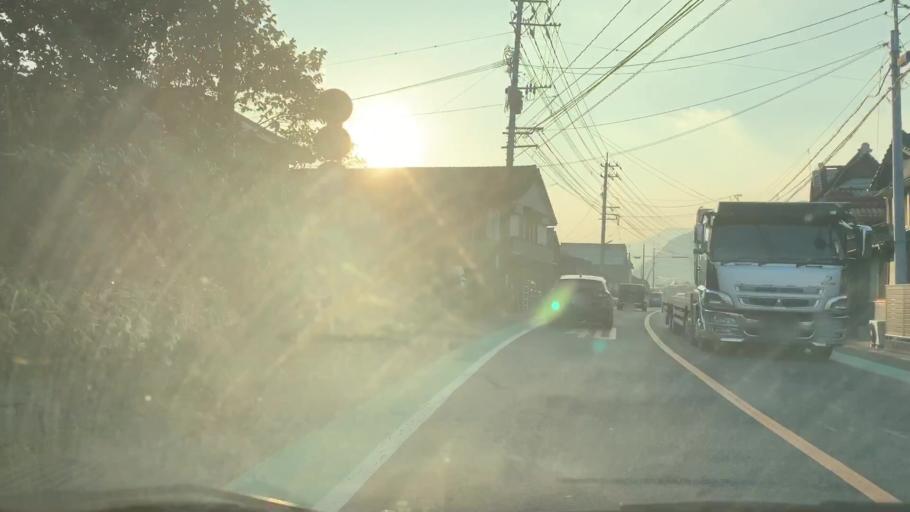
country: JP
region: Saga Prefecture
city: Takeocho-takeo
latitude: 33.2614
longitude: 130.0887
